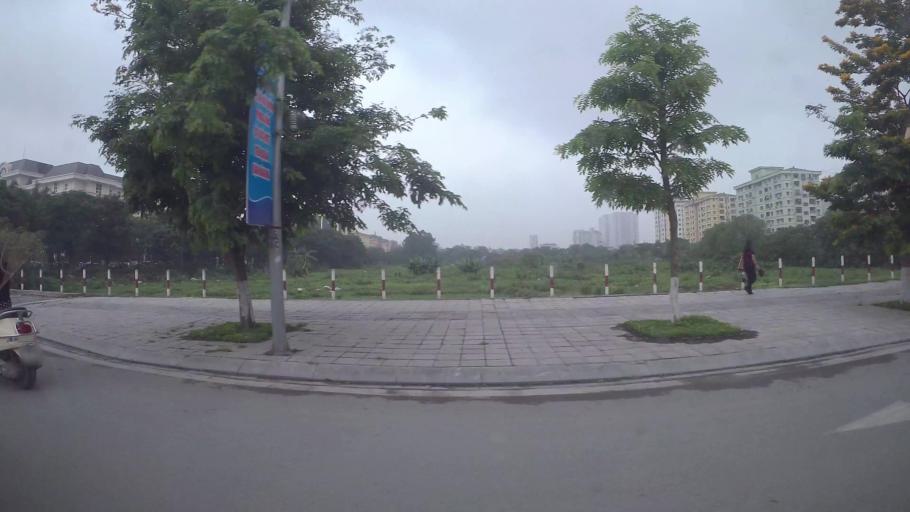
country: VN
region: Ha Noi
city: Van Dien
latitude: 20.9693
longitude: 105.8491
